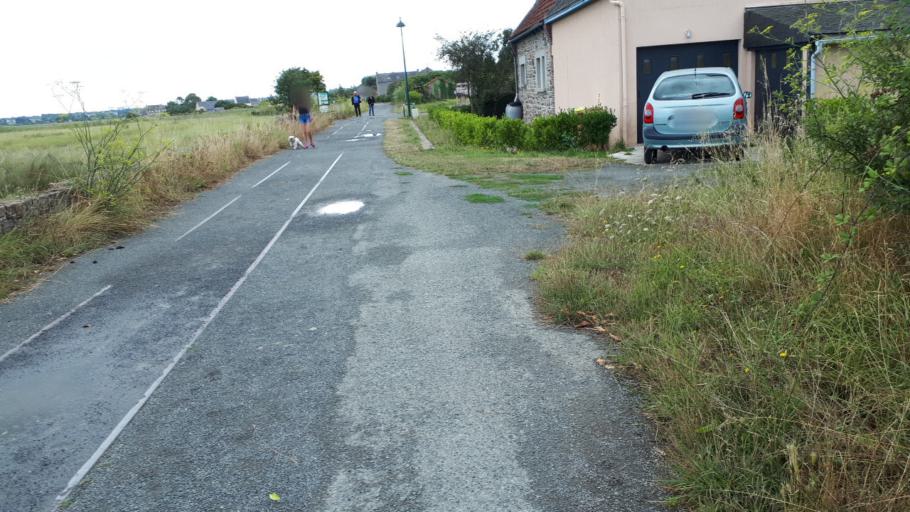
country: FR
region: Brittany
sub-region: Departement des Cotes-d'Armor
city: Langueux
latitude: 48.5065
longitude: -2.6990
